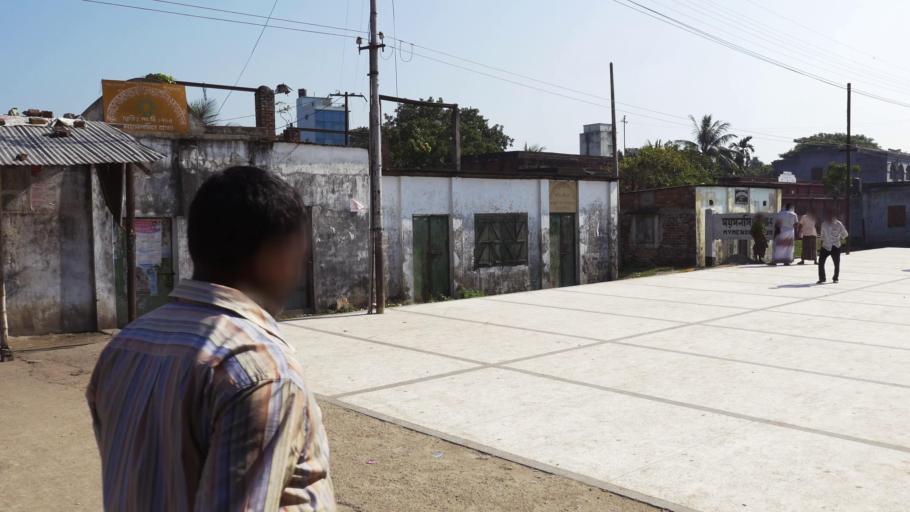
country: BD
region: Dhaka
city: Mymensingh
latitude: 24.6895
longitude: 90.4546
